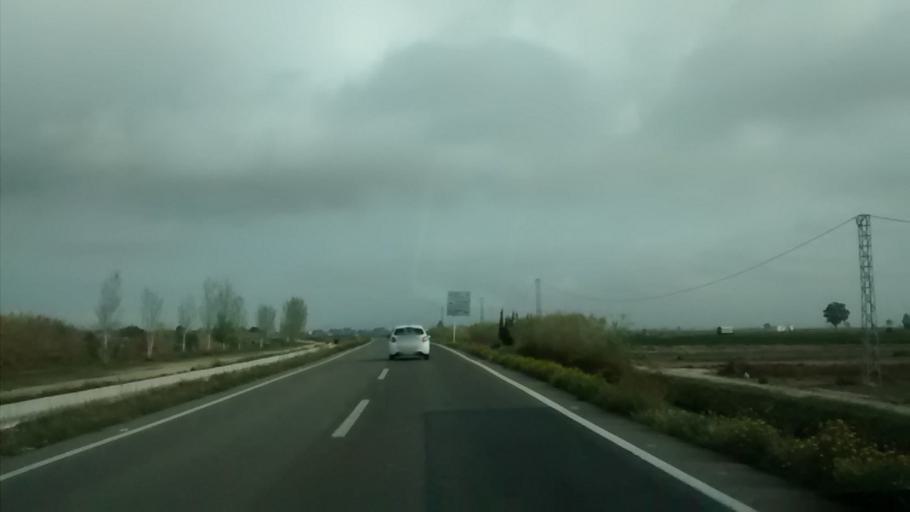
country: ES
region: Catalonia
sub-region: Provincia de Tarragona
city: Sant Carles de la Rapita
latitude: 40.6388
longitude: 0.6014
